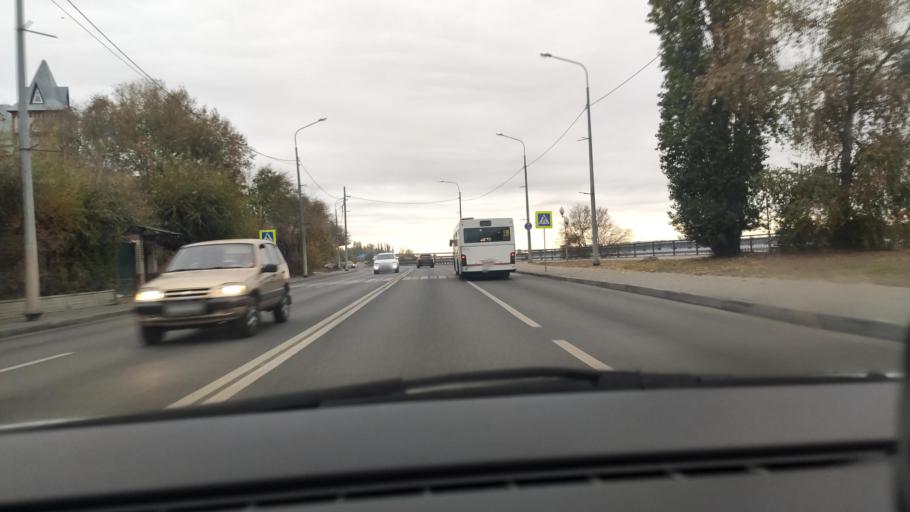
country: RU
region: Voronezj
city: Voronezh
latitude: 51.6798
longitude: 39.2278
